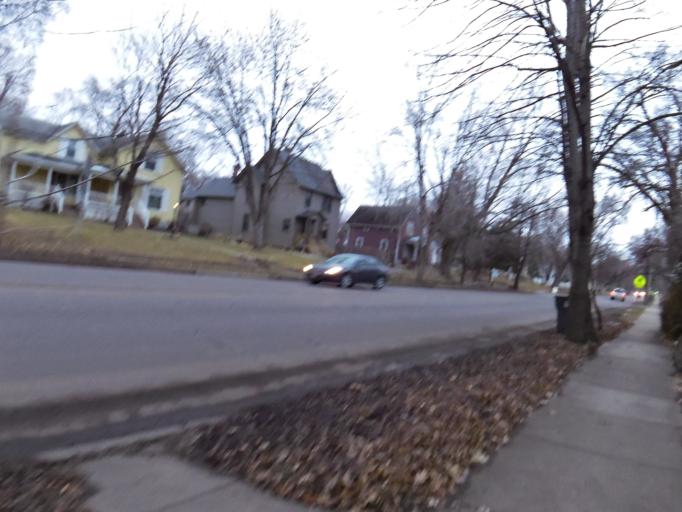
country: US
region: Wisconsin
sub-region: Saint Croix County
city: North Hudson
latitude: 44.9845
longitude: -92.7574
